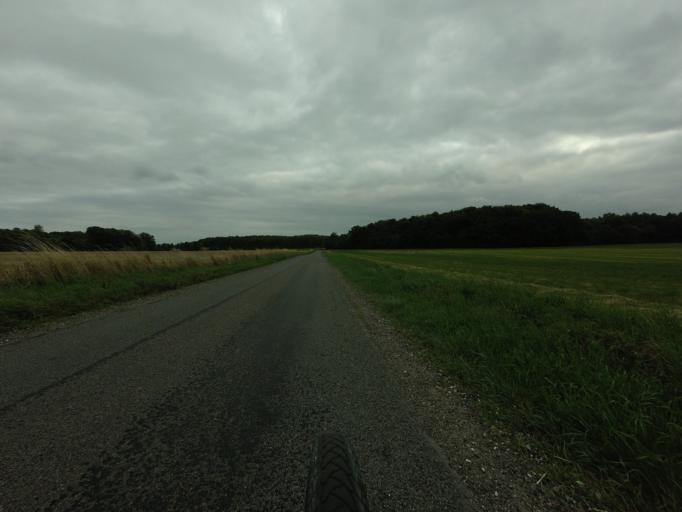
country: DK
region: Zealand
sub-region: Stevns Kommune
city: Store Heddinge
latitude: 55.3211
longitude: 12.3334
